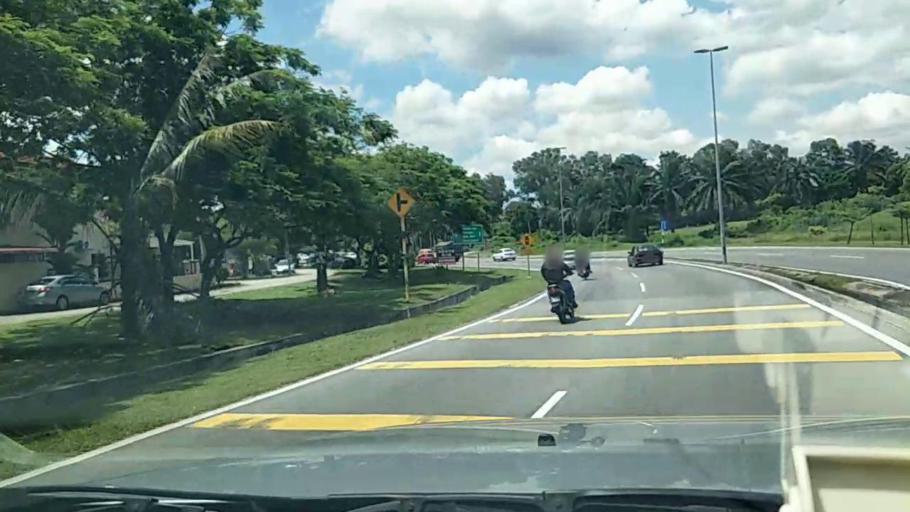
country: MY
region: Selangor
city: Subang Jaya
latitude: 2.9863
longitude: 101.6182
